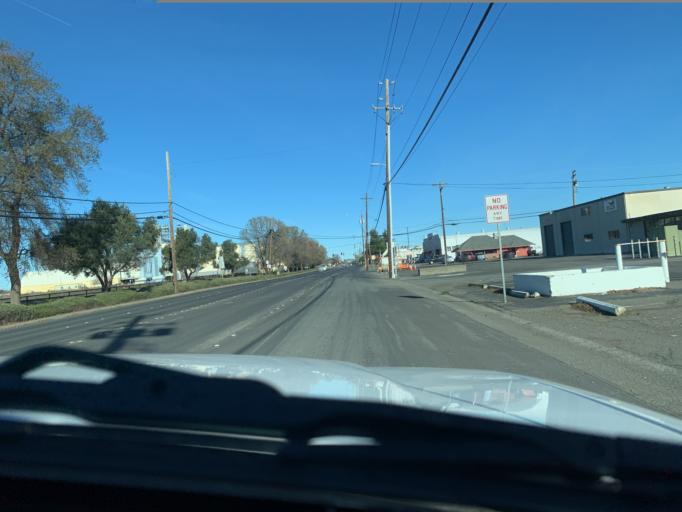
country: US
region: California
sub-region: Yolo County
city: Woodland
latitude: 38.6891
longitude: -121.7652
